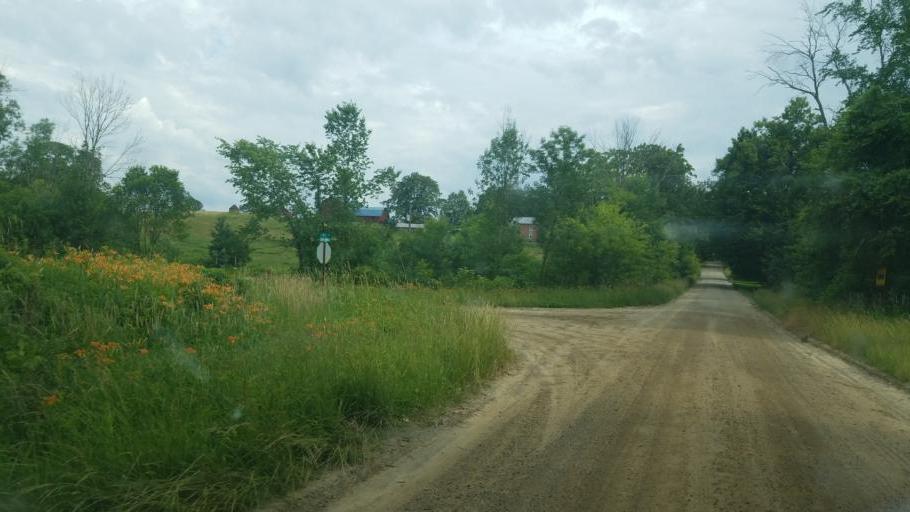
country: US
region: Michigan
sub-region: Barry County
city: Nashville
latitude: 42.6119
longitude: -84.9757
